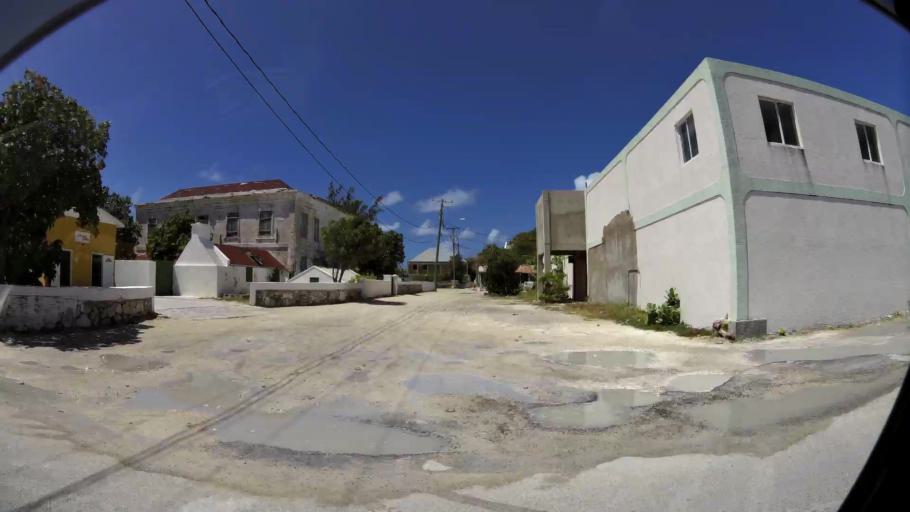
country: TC
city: Cockburn Town
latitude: 21.4711
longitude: -71.1462
